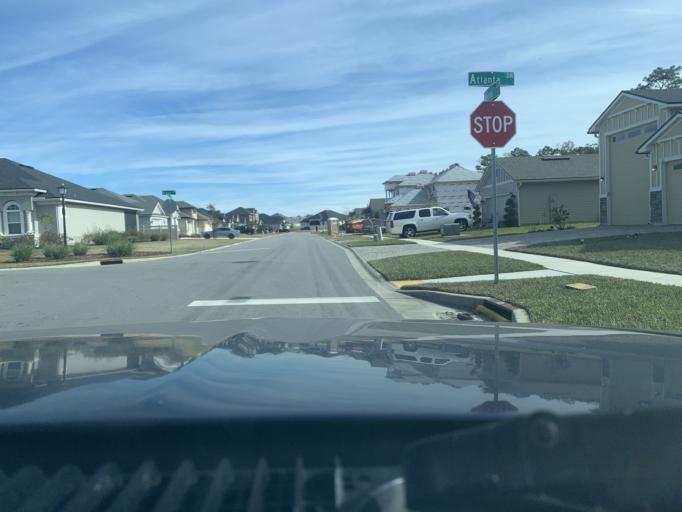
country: US
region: Florida
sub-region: Clay County
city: Green Cove Springs
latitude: 29.9768
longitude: -81.5274
